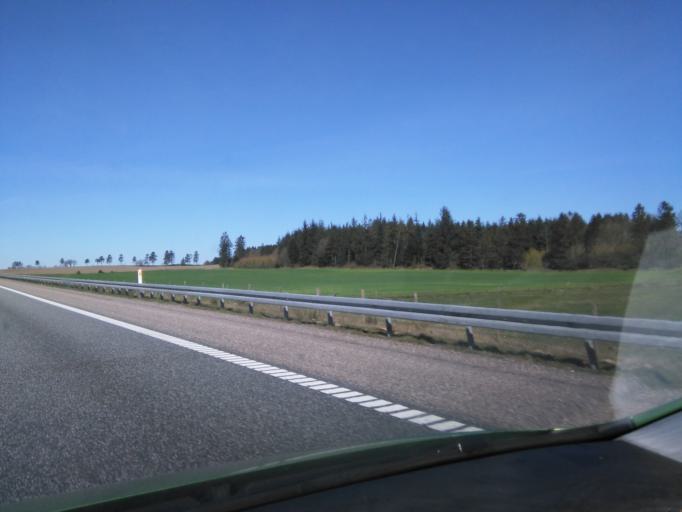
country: DK
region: South Denmark
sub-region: Vejle Kommune
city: Give
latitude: 55.8342
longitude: 9.3382
